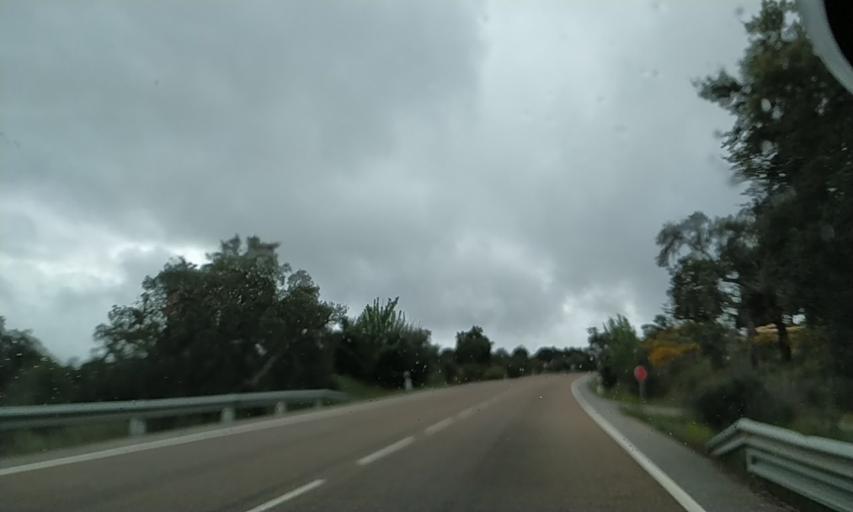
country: ES
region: Extremadura
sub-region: Provincia de Badajoz
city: Puebla de Obando
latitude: 39.2391
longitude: -6.5640
